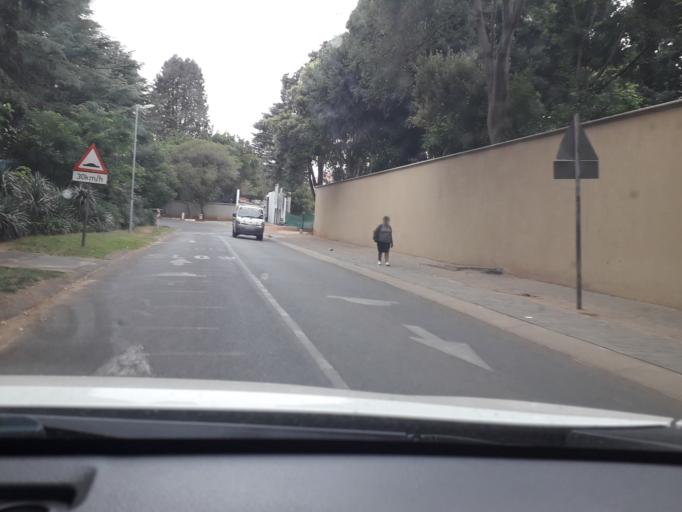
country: ZA
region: Gauteng
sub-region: City of Johannesburg Metropolitan Municipality
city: Johannesburg
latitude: -26.1174
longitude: 28.0414
